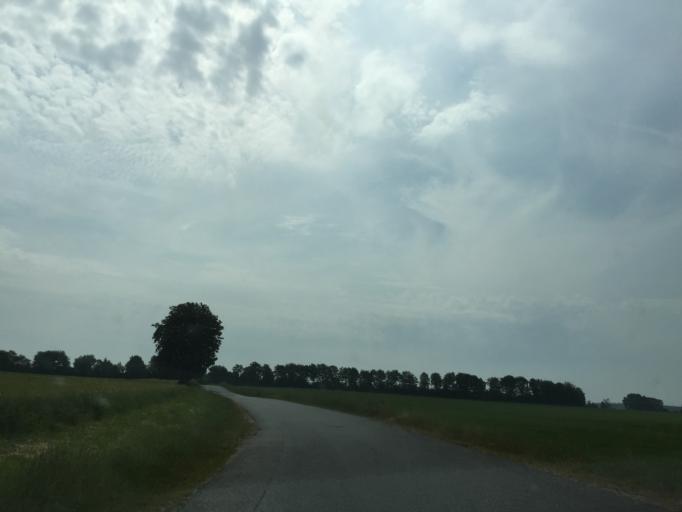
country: DK
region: Central Jutland
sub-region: Silkeborg Kommune
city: Virklund
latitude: 56.0972
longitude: 9.4662
